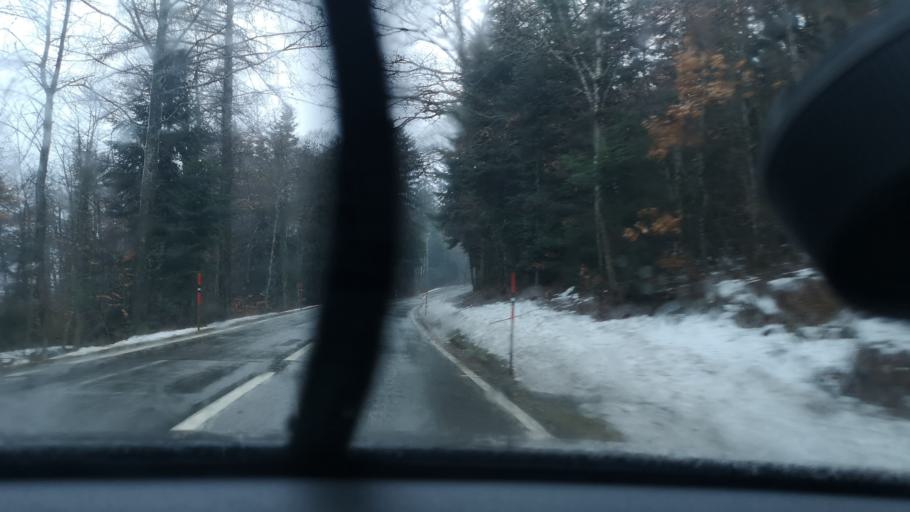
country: CH
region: Neuchatel
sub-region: Boudry District
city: Boudry
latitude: 46.9807
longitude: 6.8287
